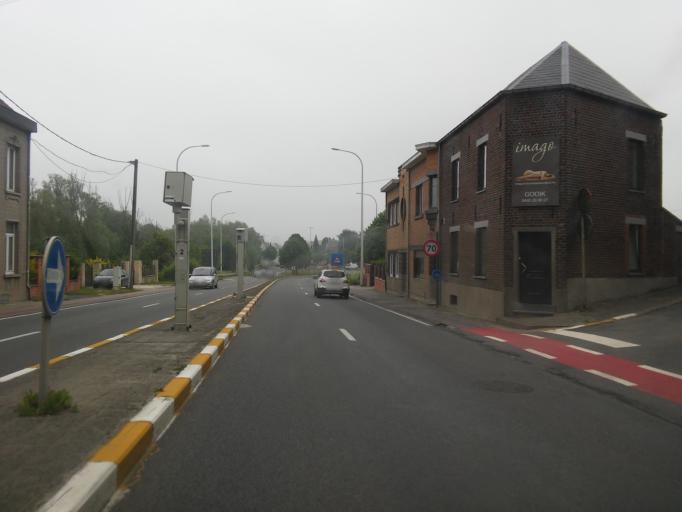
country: BE
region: Flanders
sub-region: Provincie Vlaams-Brabant
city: Dilbeek
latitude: 50.8401
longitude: 4.2183
